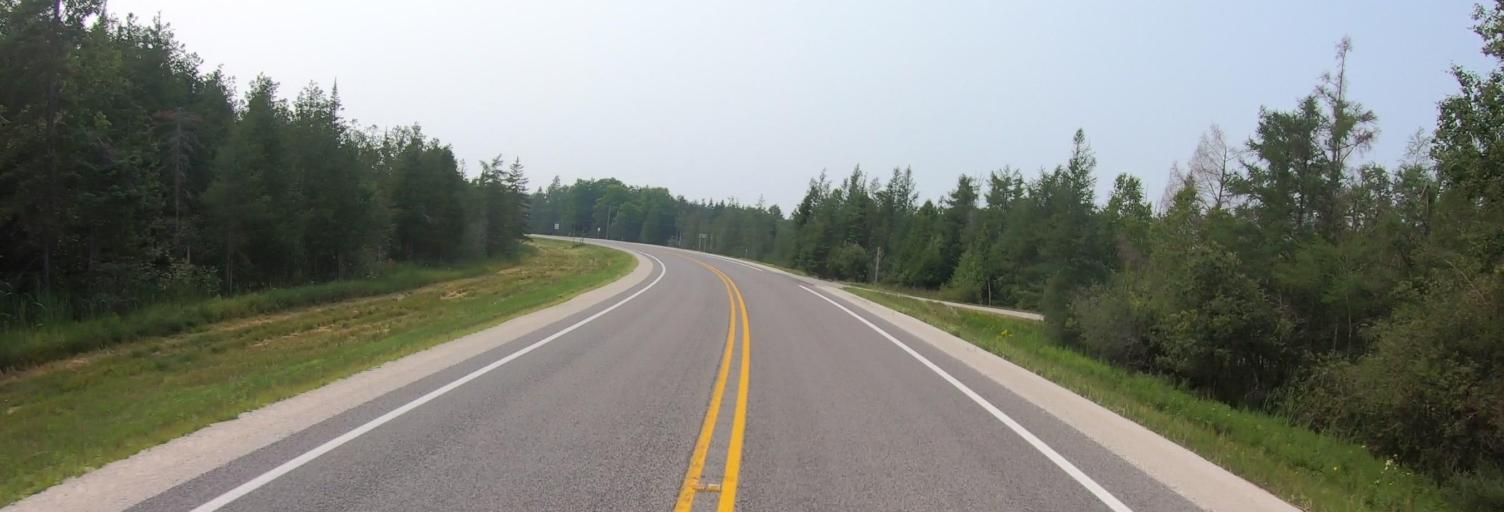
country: US
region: Michigan
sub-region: Chippewa County
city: Sault Ste. Marie
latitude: 46.0719
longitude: -84.0944
